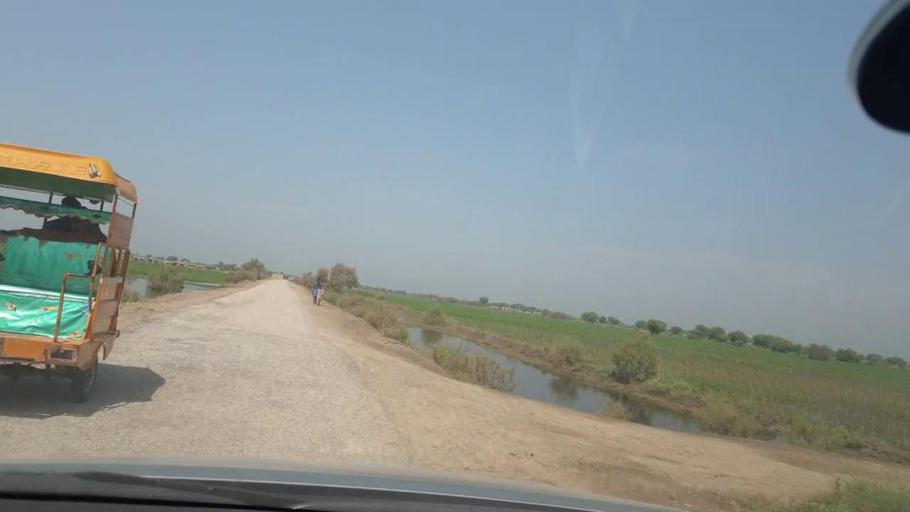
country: PK
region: Balochistan
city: Mehrabpur
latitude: 28.0690
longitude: 68.0546
